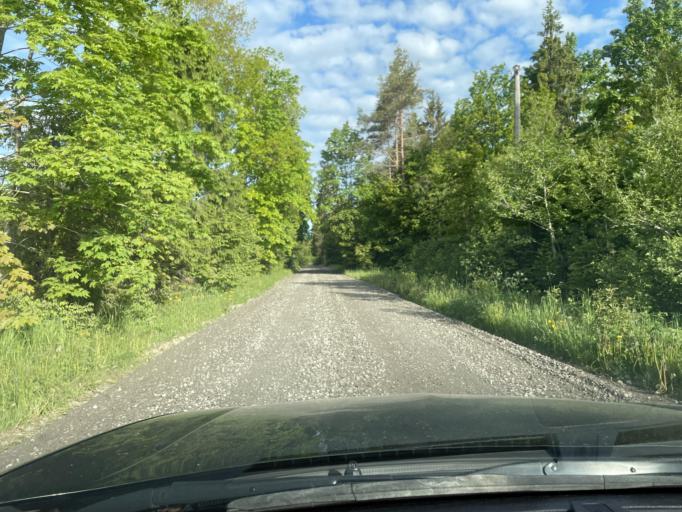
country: EE
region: Harju
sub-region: Keila linn
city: Keila
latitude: 59.3013
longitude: 24.3078
